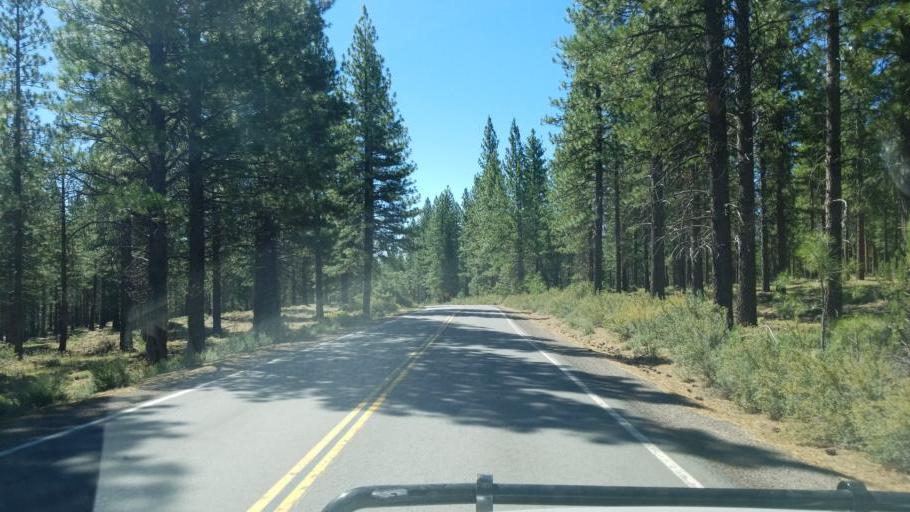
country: US
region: California
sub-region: Lassen County
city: Susanville
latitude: 40.4309
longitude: -120.7305
